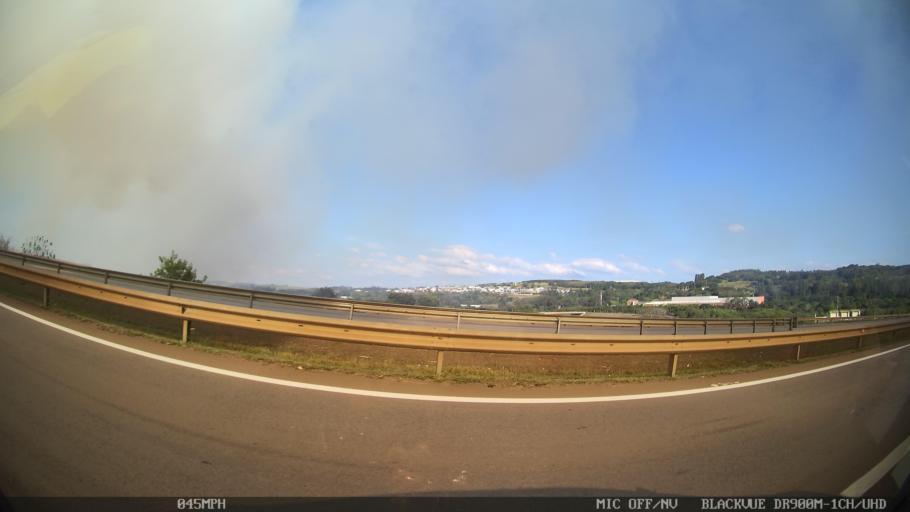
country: BR
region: Sao Paulo
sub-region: Piracicaba
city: Piracicaba
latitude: -22.6955
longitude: -47.6041
